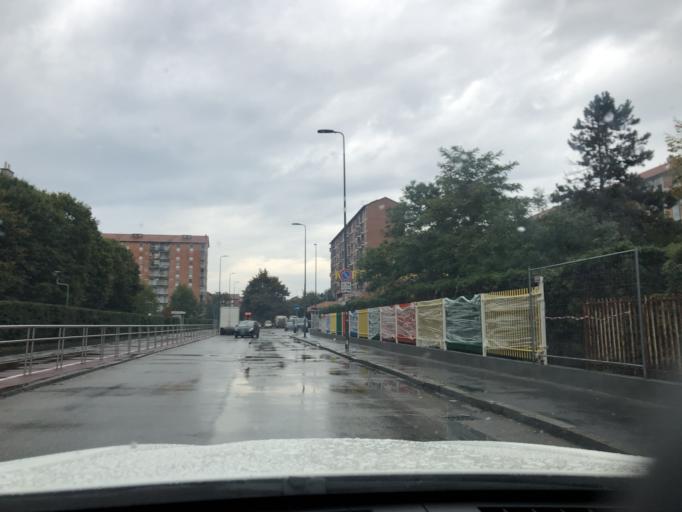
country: IT
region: Lombardy
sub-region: Citta metropolitana di Milano
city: Baranzate
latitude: 45.4903
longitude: 9.1226
